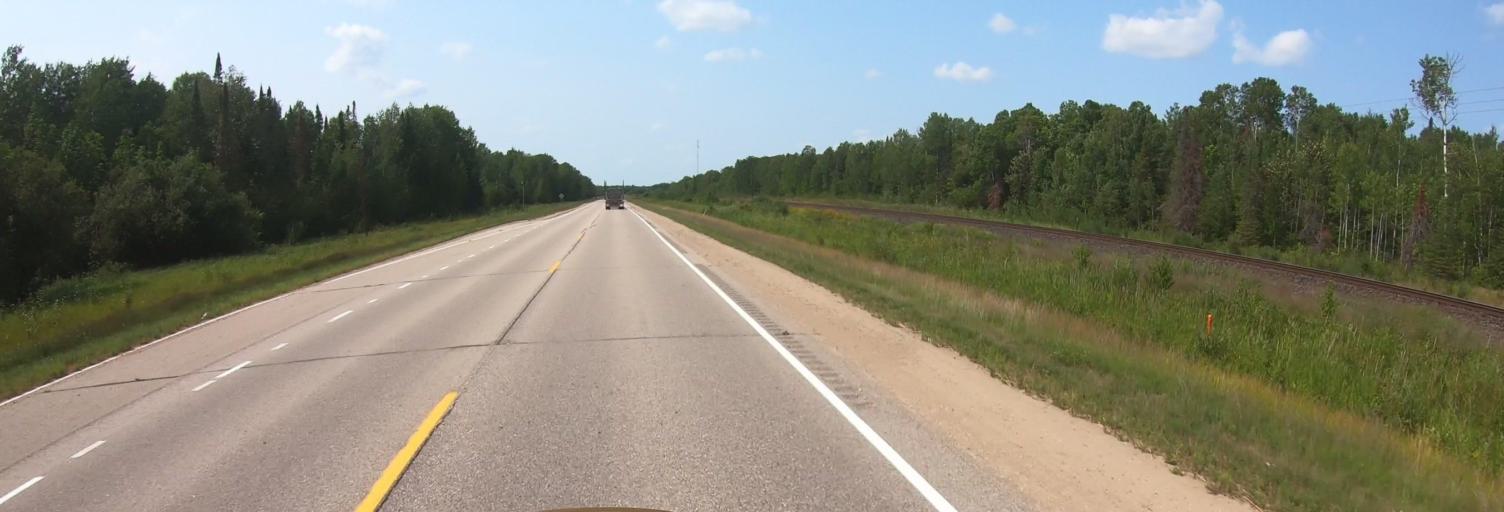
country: US
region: Minnesota
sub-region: Roseau County
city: Warroad
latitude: 48.7939
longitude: -95.0697
